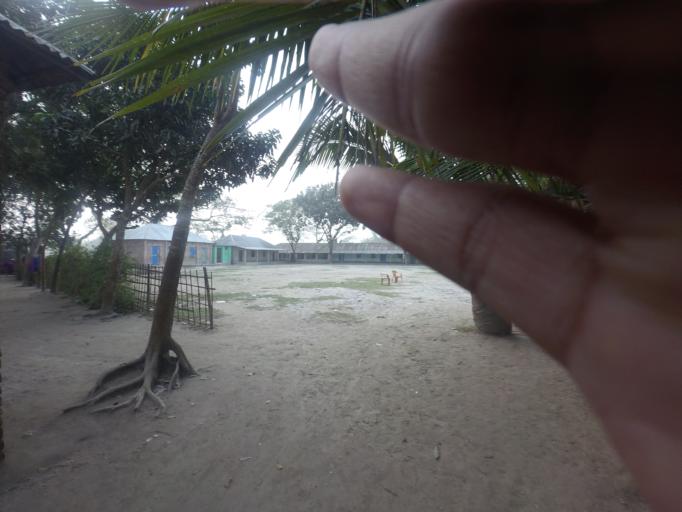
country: BD
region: Rajshahi
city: Saidpur
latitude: 25.9178
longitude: 88.9429
